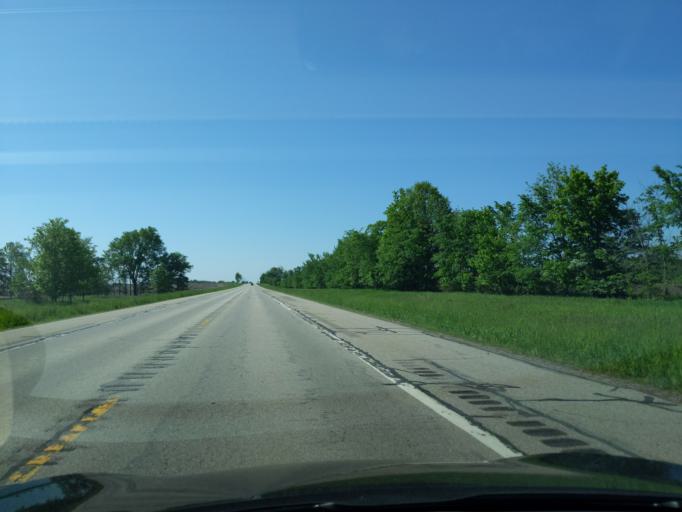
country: US
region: Michigan
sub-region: Ingham County
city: Webberville
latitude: 42.5785
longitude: -84.1926
